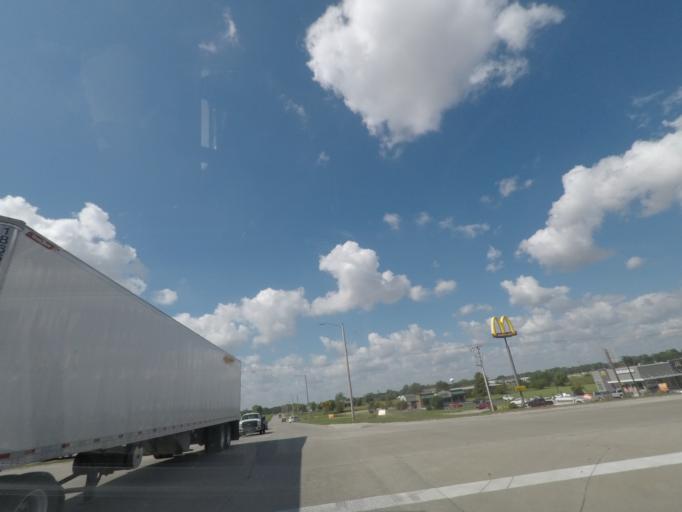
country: US
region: Iowa
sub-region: Story County
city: Nevada
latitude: 42.0098
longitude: -93.4348
